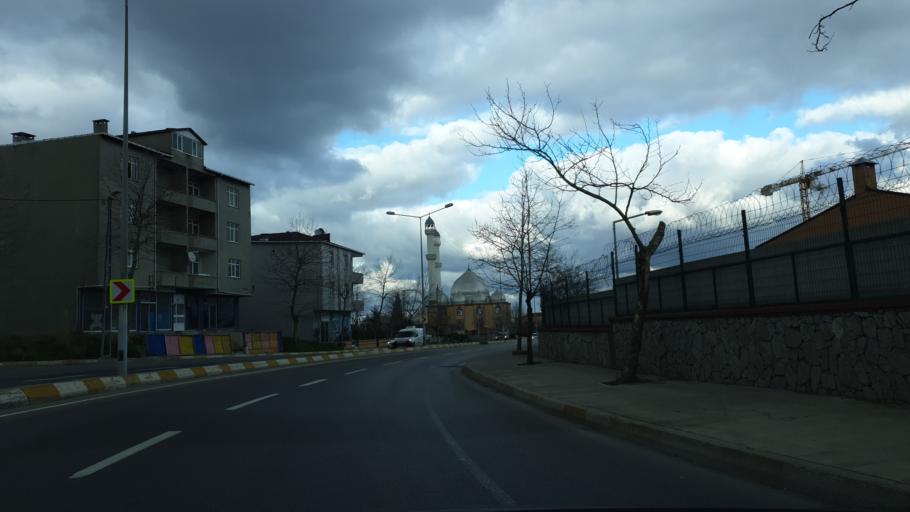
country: TR
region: Istanbul
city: Sultanbeyli
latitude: 40.9344
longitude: 29.2800
